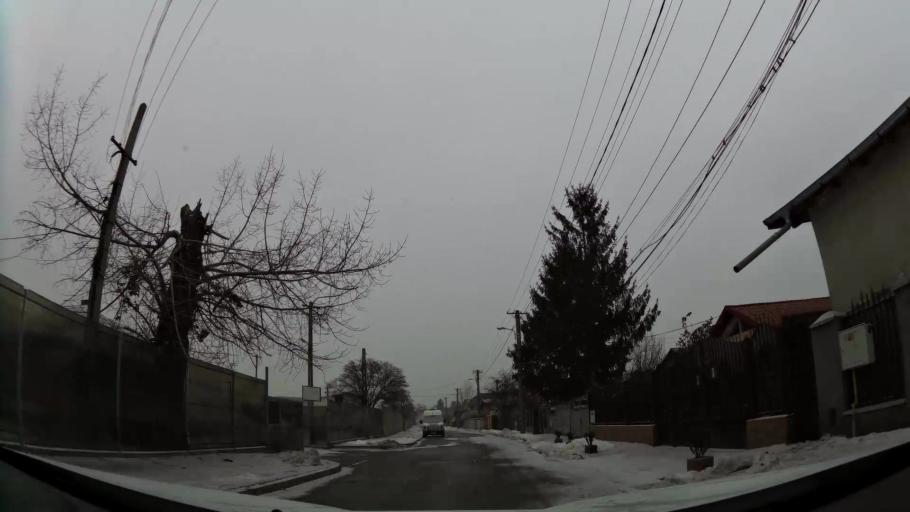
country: RO
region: Prahova
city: Ploiesti
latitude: 44.9514
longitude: 26.0334
